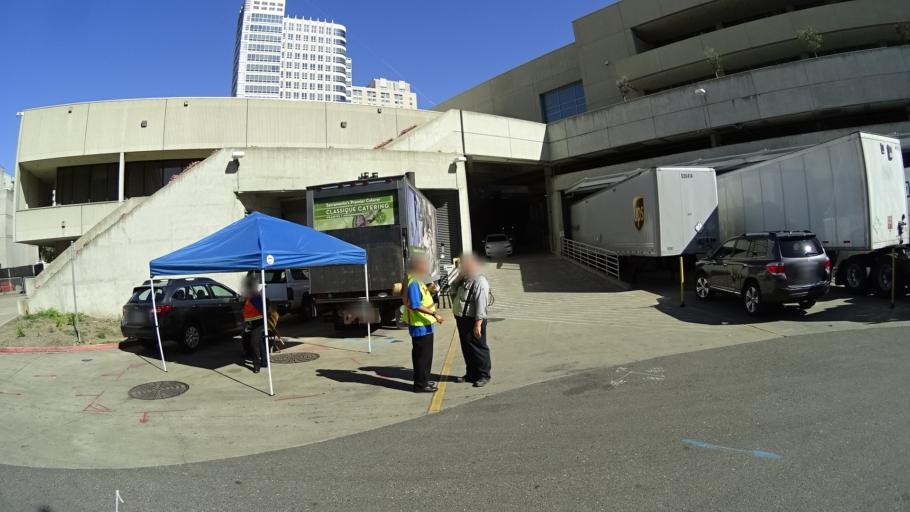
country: US
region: California
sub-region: Sacramento County
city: Sacramento
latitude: 38.5777
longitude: -121.4884
